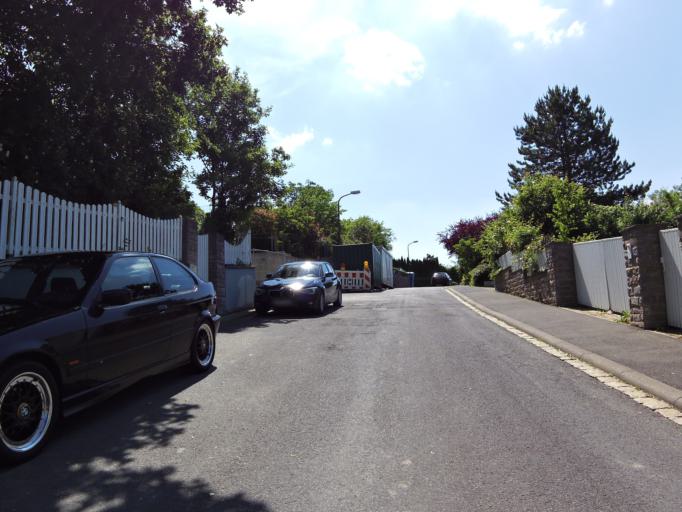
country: DE
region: Bavaria
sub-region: Regierungsbezirk Unterfranken
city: Wuerzburg
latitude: 49.7772
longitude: 9.9489
